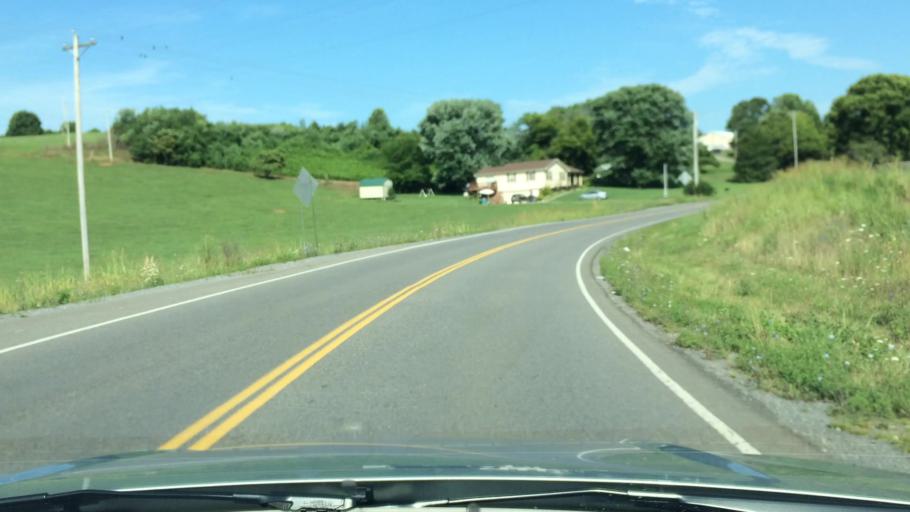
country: US
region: Tennessee
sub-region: Jefferson County
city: White Pine
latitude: 36.1494
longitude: -83.3441
